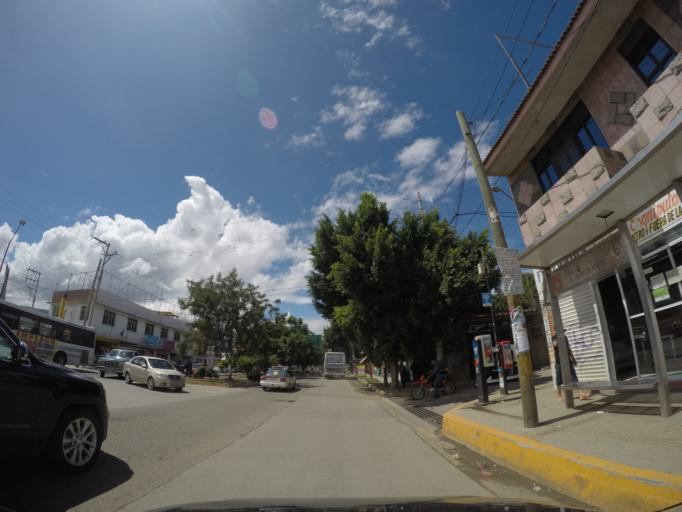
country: MX
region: Oaxaca
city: Oaxaca de Juarez
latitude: 17.0486
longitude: -96.7314
